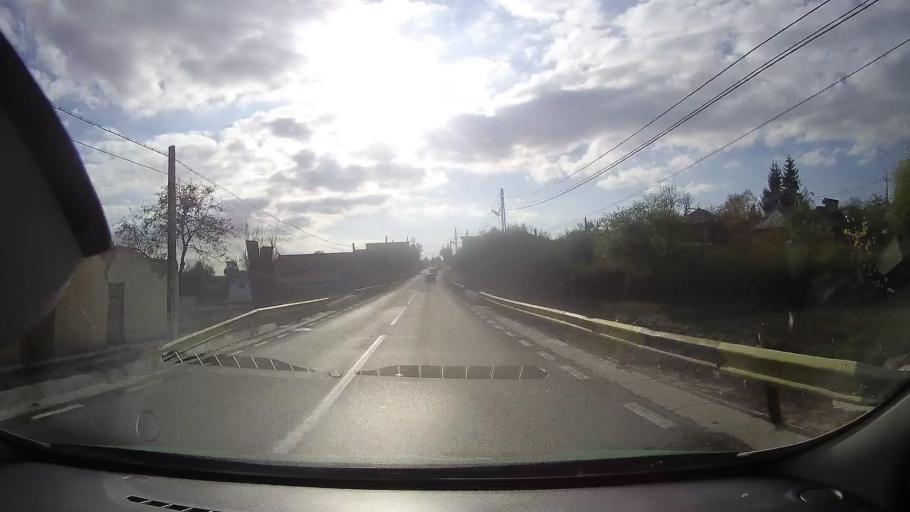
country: RO
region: Tulcea
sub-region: Comuna Topolog
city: Topolog
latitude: 44.8816
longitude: 28.3781
